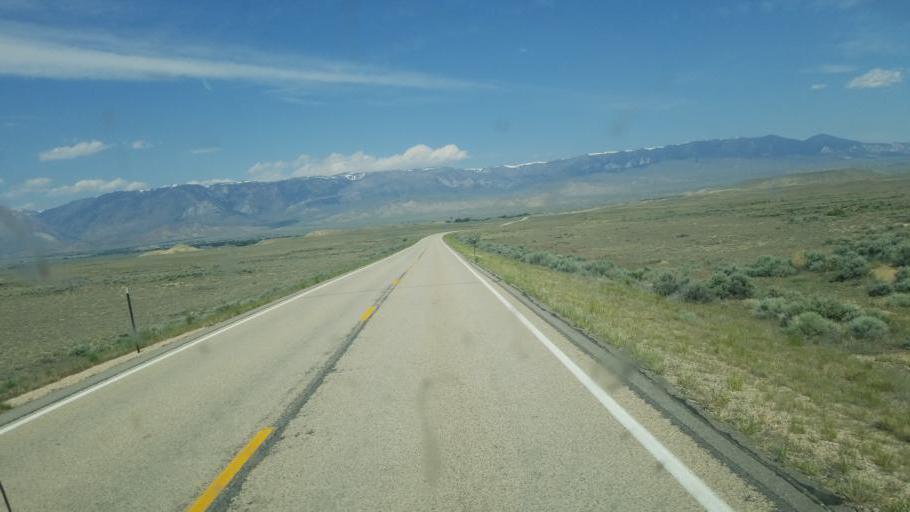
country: US
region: Montana
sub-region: Carbon County
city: Red Lodge
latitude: 44.8904
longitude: -109.0812
